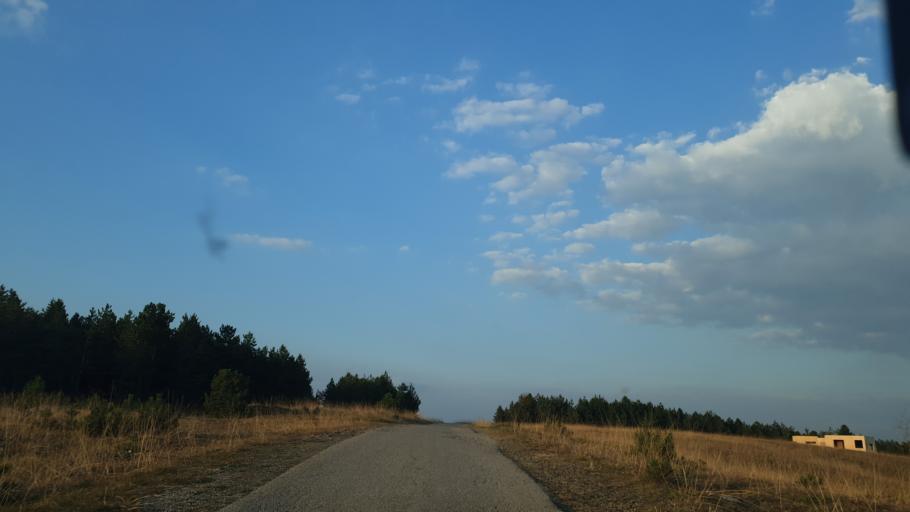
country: RS
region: Central Serbia
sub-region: Zlatiborski Okrug
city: Kosjeric
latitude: 44.0188
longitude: 20.0017
